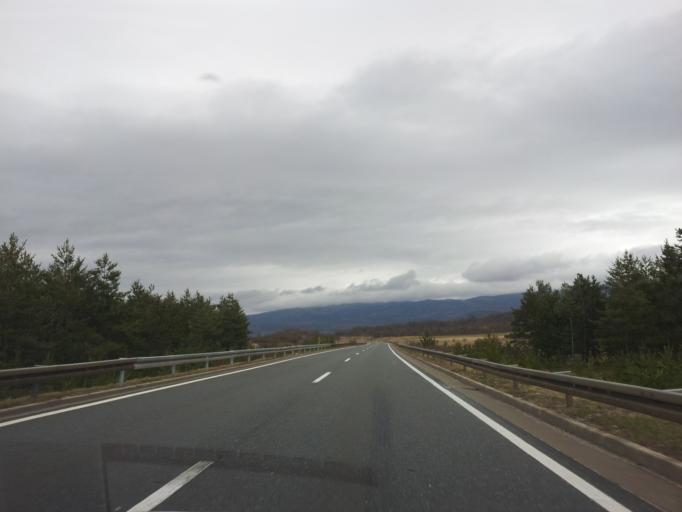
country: HR
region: Zadarska
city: Gracac
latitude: 44.5233
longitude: 15.7465
